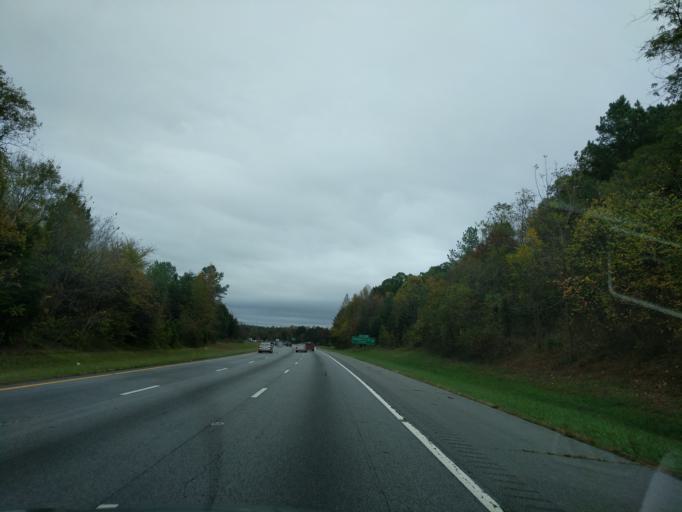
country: US
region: North Carolina
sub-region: Randolph County
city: Trinity
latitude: 35.8708
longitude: -80.0120
